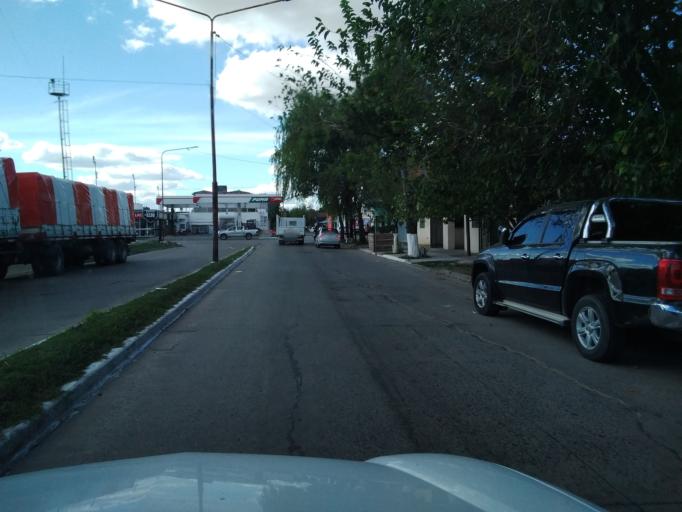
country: AR
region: Corrientes
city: Corrientes
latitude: -27.4860
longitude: -58.8379
